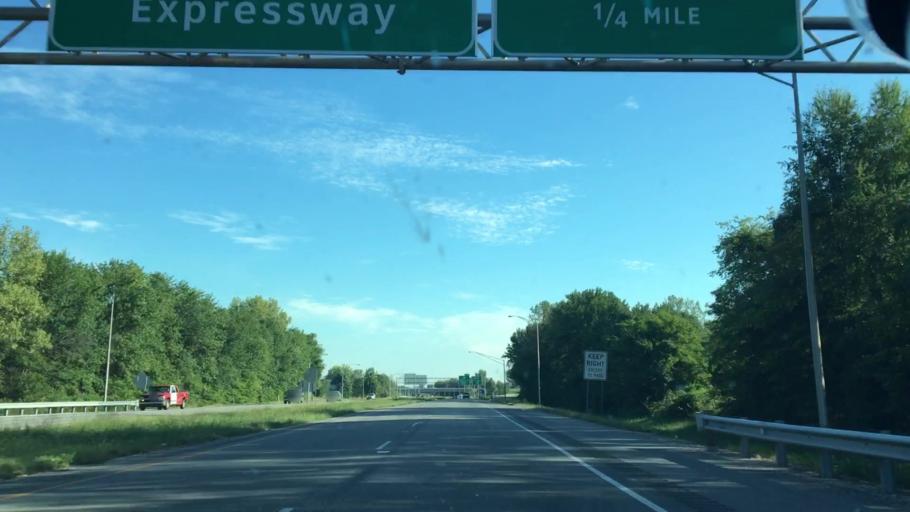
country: US
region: Kentucky
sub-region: Daviess County
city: Owensboro
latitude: 37.7726
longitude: -87.1657
